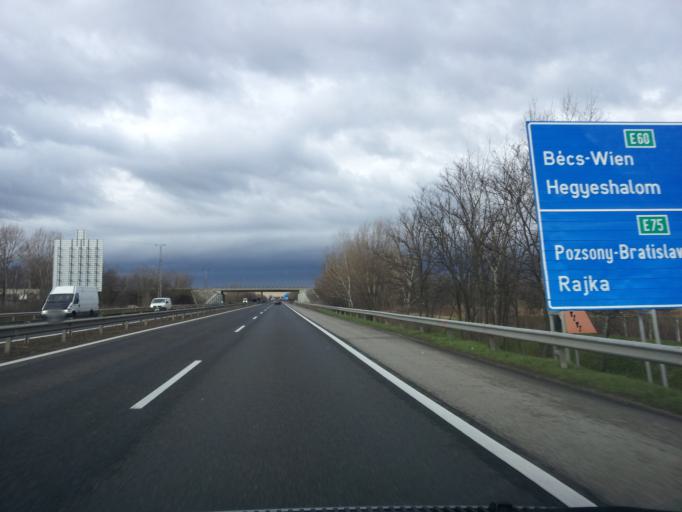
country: HU
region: Gyor-Moson-Sopron
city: Gyorujbarat
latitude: 47.6383
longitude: 17.6420
